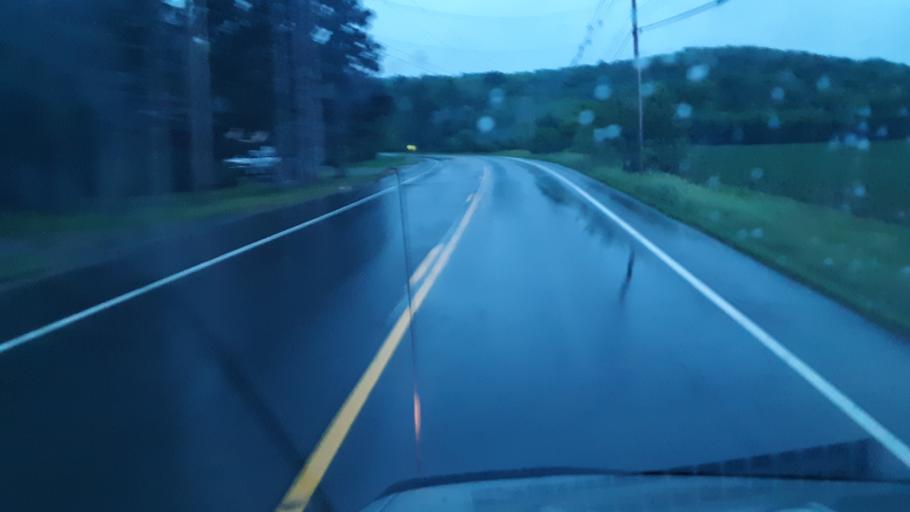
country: US
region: Maine
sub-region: Penobscot County
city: Patten
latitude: 45.8902
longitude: -68.4238
